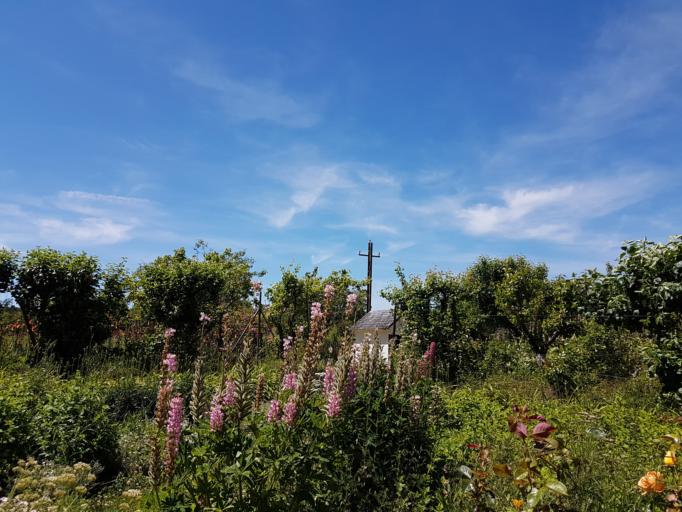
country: FR
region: Bourgogne
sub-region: Departement de Saone-et-Loire
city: Epinac
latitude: 47.0104
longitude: 4.4717
